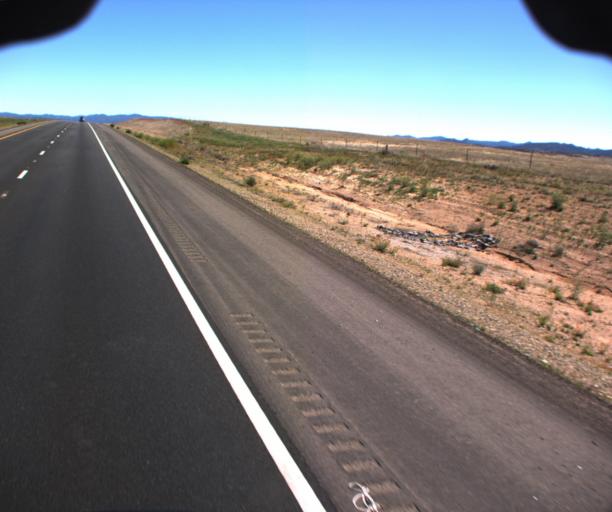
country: US
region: Arizona
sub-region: Yavapai County
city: Chino Valley
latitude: 34.6981
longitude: -112.4486
